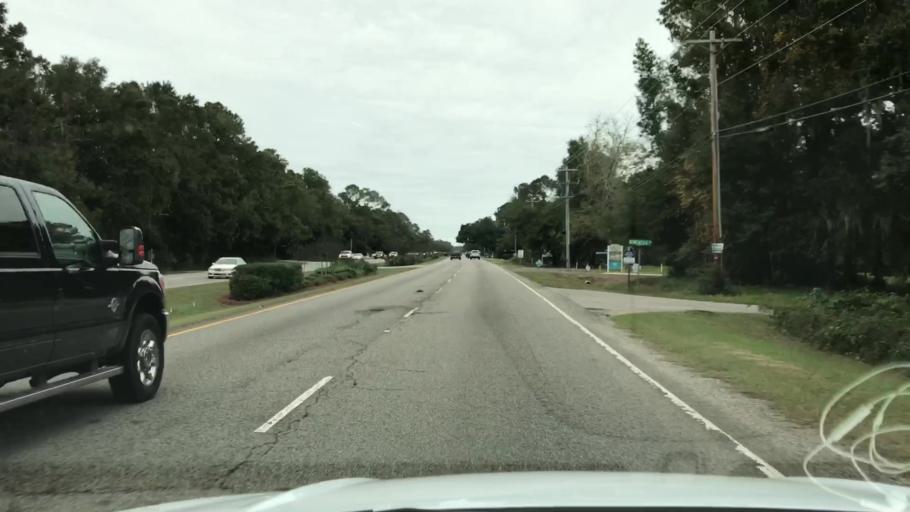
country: US
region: South Carolina
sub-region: Georgetown County
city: Murrells Inlet
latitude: 33.4616
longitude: -79.1113
